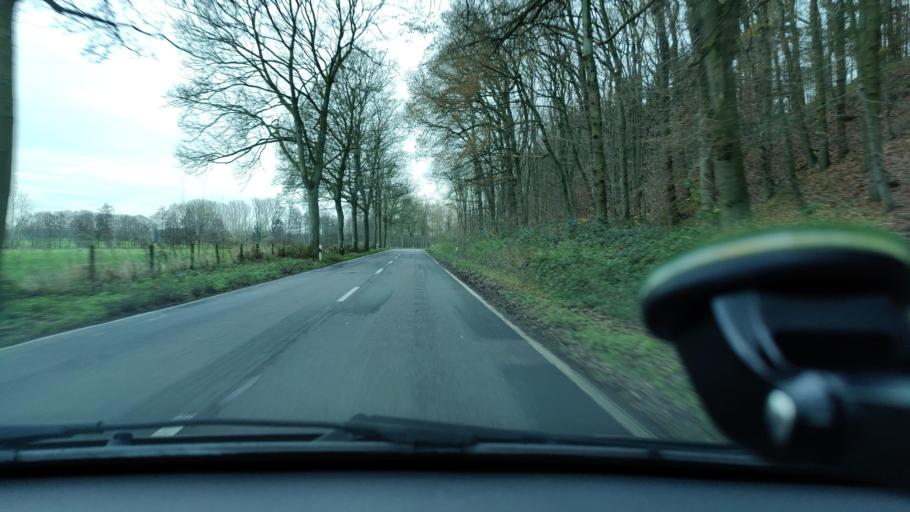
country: DE
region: North Rhine-Westphalia
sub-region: Regierungsbezirk Dusseldorf
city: Sonsbeck
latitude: 51.6835
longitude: 6.3812
